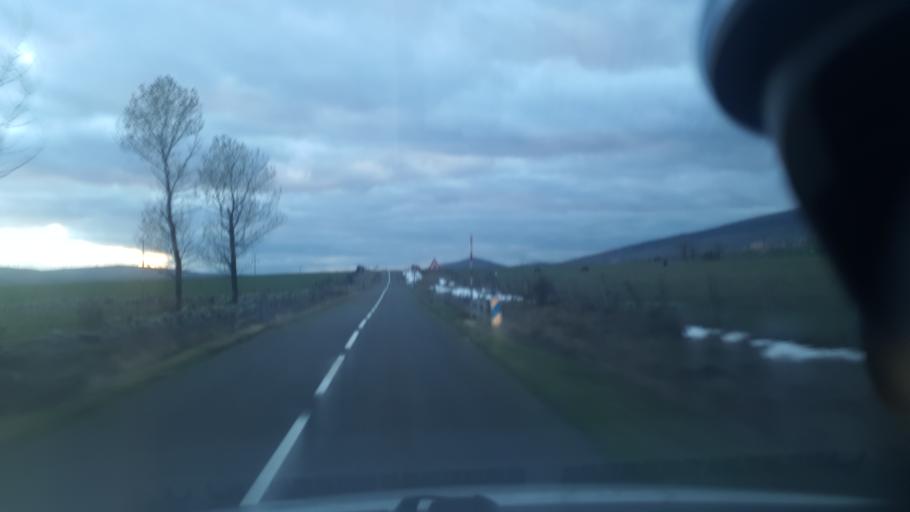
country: ES
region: Castille and Leon
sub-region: Provincia de Segovia
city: Villacastin
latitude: 40.6950
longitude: -4.4040
